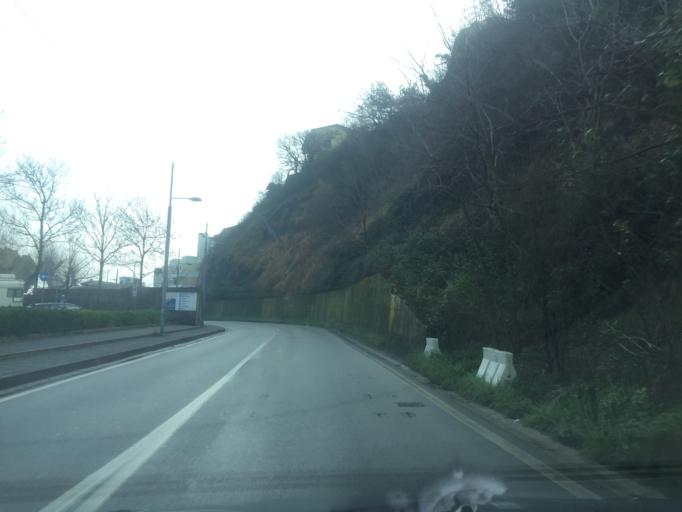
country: IT
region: Friuli Venezia Giulia
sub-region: Provincia di Trieste
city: Muggia
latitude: 45.6067
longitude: 13.7576
